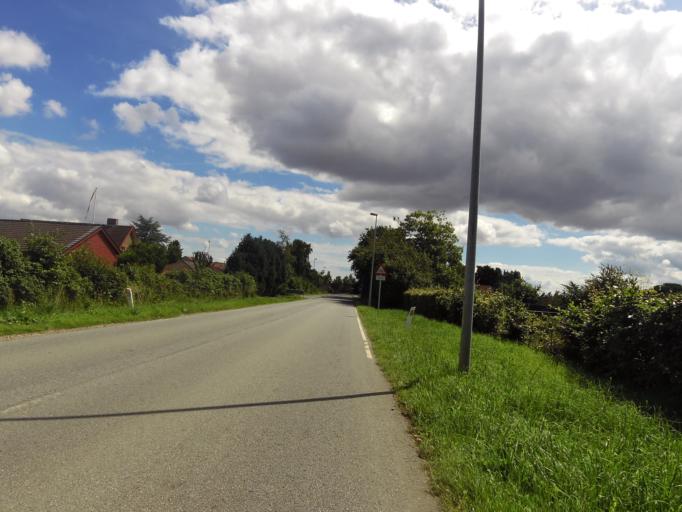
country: DK
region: South Denmark
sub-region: Haderslev Kommune
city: Haderslev
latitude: 55.2538
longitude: 9.4545
